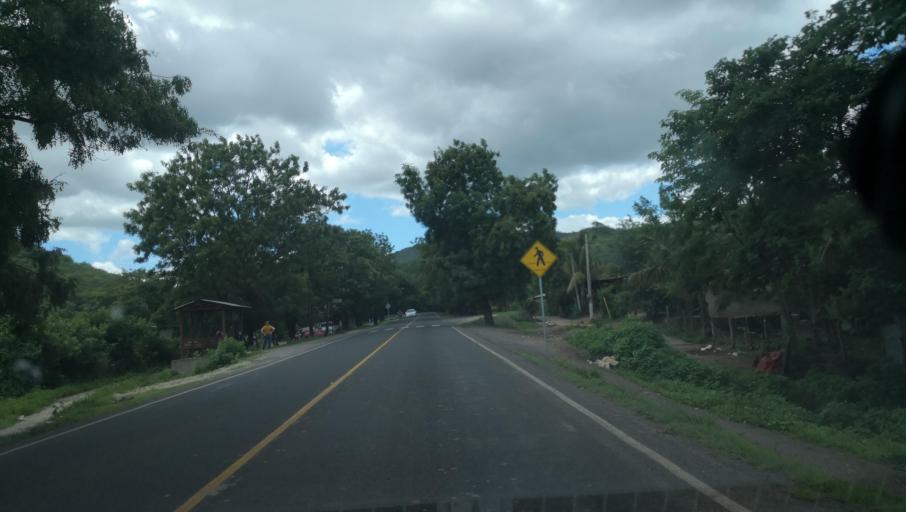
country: NI
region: Madriz
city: Palacaguina
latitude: 13.4552
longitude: -86.4518
